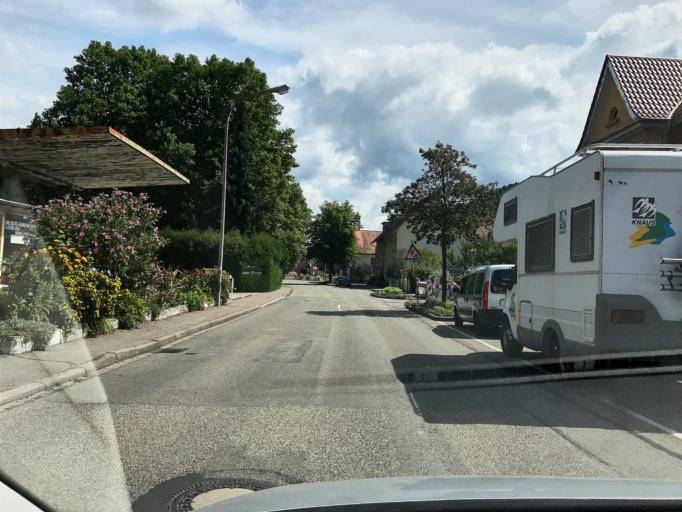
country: DE
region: Baden-Wuerttemberg
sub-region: Freiburg Region
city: Muhlenbach
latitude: 48.2774
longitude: 8.0938
